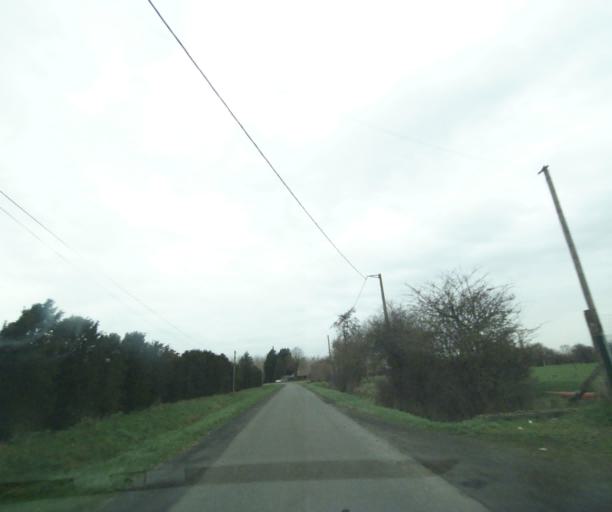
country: FR
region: Nord-Pas-de-Calais
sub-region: Departement du Nord
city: Vicq
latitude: 50.4206
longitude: 3.6168
